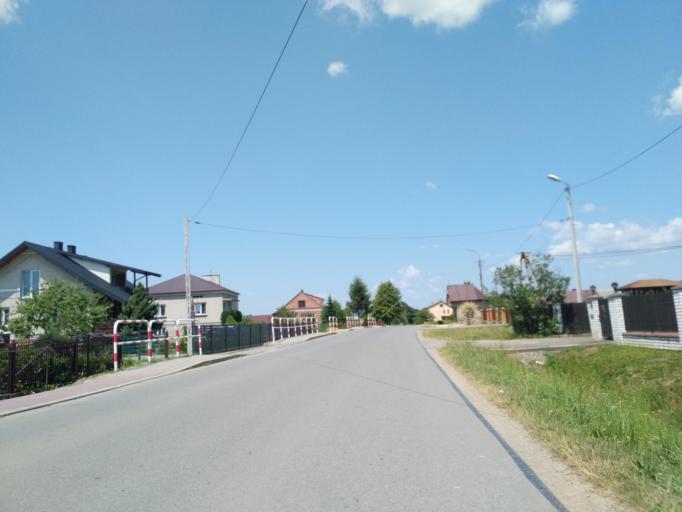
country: PL
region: Subcarpathian Voivodeship
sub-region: Powiat sanocki
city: Niebieszczany
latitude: 49.5018
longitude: 22.1580
